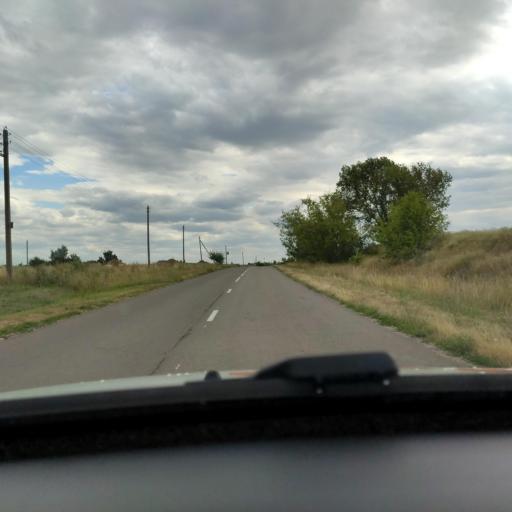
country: RU
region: Voronezj
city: Orlovo
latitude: 51.6791
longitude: 39.5741
